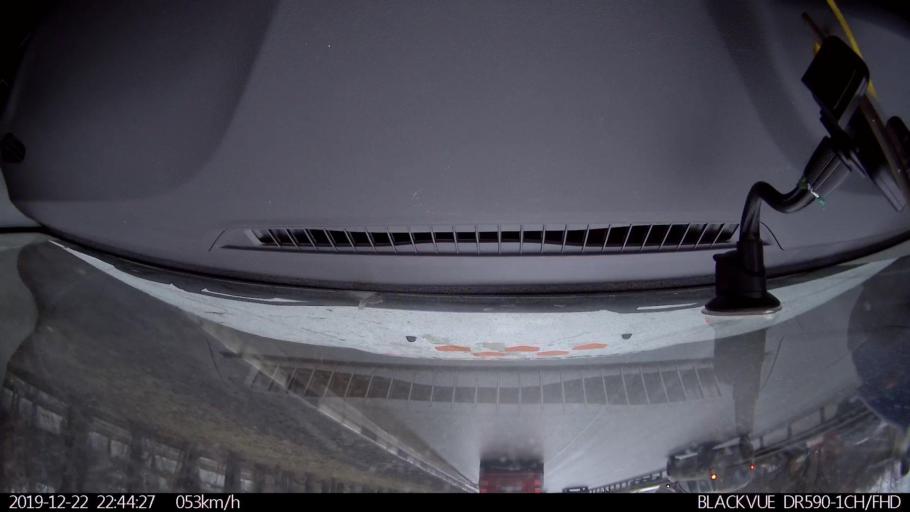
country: RU
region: Nizjnij Novgorod
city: Nizhniy Novgorod
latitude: 56.2742
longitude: 43.9063
